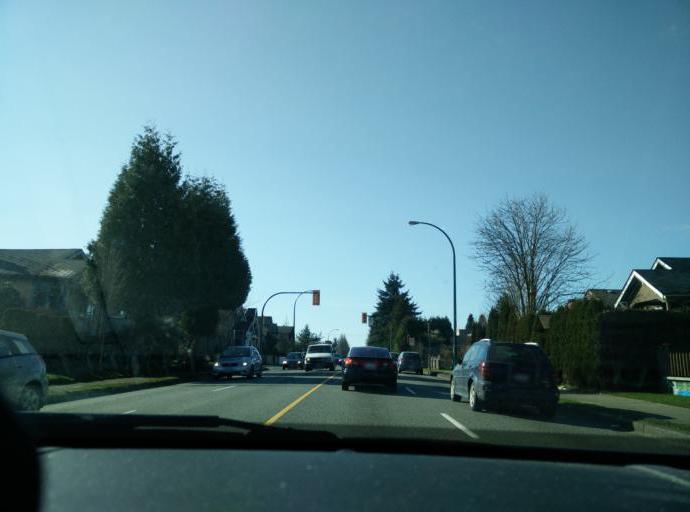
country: CA
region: British Columbia
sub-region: Fraser Valley Regional District
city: North Vancouver
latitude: 49.2696
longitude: -123.0592
